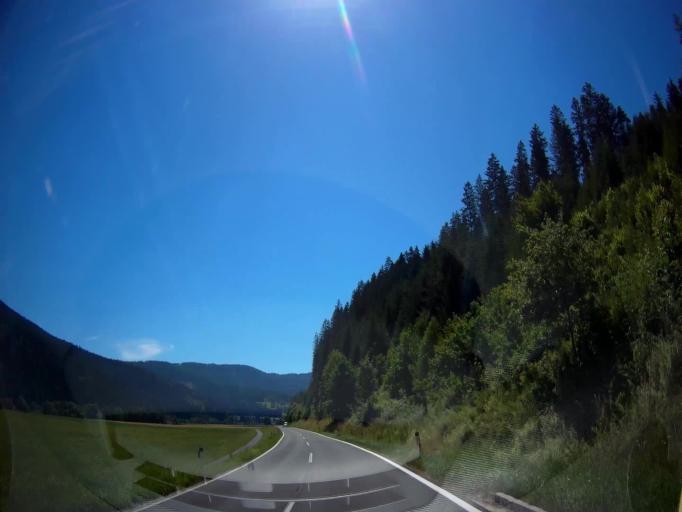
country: AT
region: Carinthia
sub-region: Politischer Bezirk Sankt Veit an der Glan
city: Gurk
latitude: 46.8548
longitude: 14.2143
